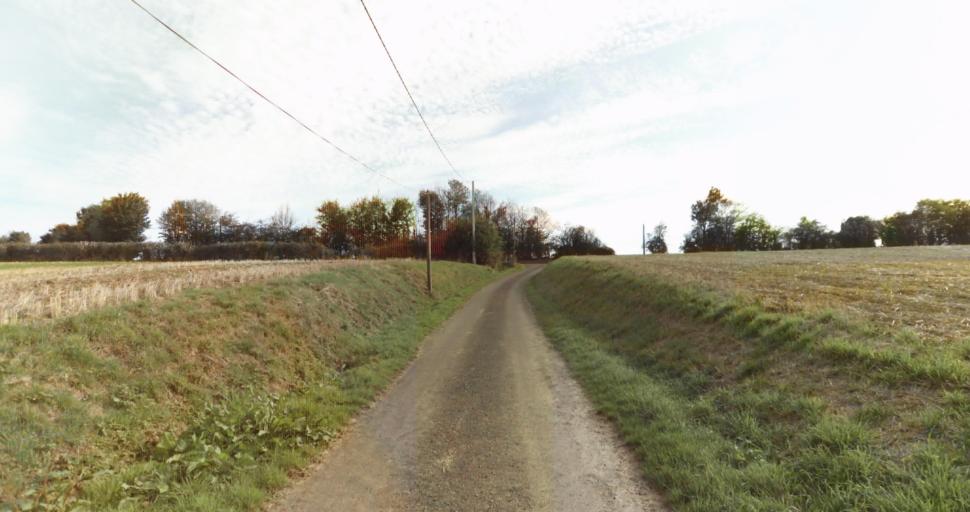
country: FR
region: Lower Normandy
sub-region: Departement de l'Orne
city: Gace
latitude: 48.7126
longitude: 0.2579
